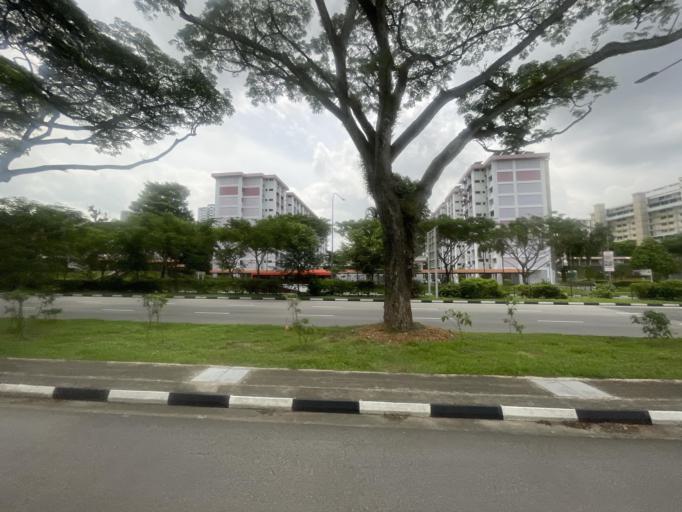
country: SG
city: Singapore
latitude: 1.3158
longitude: 103.7720
